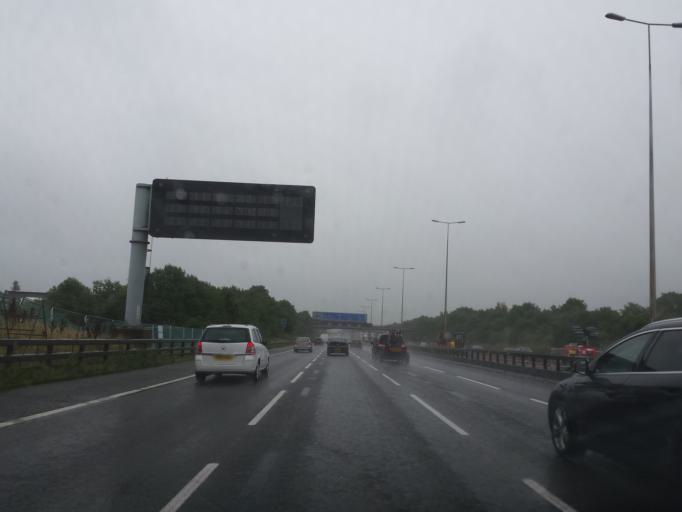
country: GB
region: England
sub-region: Leicestershire
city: Enderby
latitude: 52.6136
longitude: -1.2015
